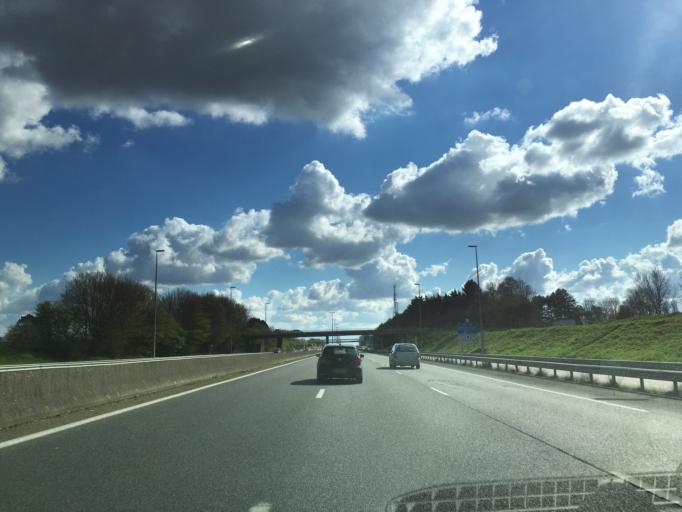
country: FR
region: Nord-Pas-de-Calais
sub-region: Departement du Pas-de-Calais
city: Fampoux
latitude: 50.2686
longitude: 2.8678
